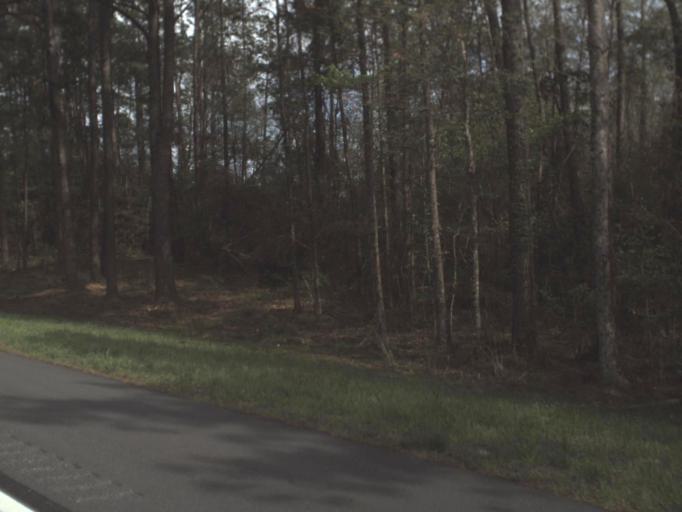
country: US
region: Florida
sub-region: Walton County
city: DeFuniak Springs
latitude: 30.6990
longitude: -85.9747
